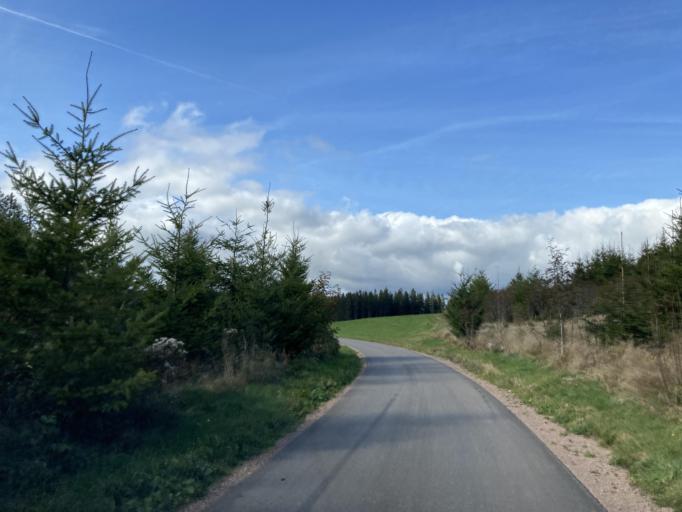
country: DE
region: Baden-Wuerttemberg
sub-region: Freiburg Region
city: Vohrenbach
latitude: 48.0798
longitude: 8.2811
